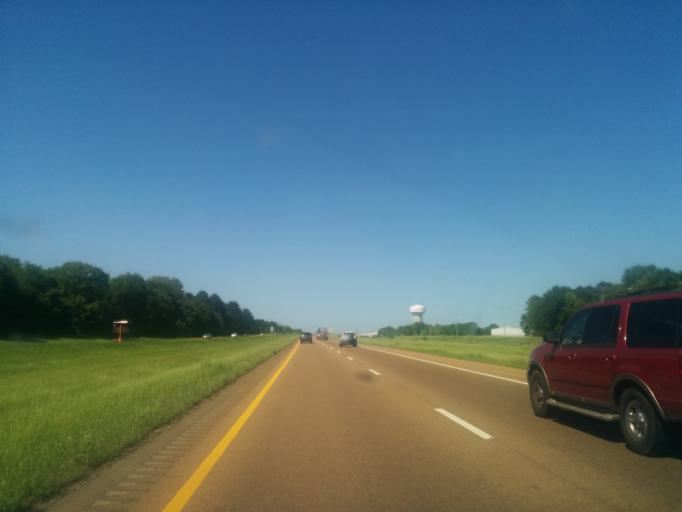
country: US
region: Mississippi
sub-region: Madison County
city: Canton
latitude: 32.5563
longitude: -90.0843
